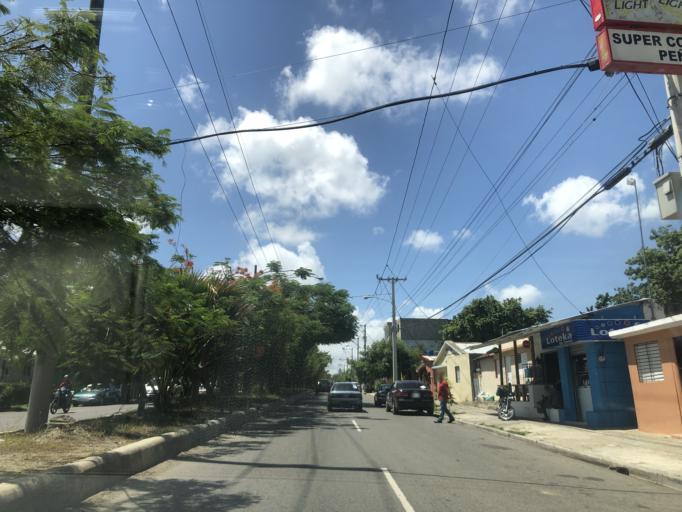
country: DO
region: Santiago
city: Santiago de los Caballeros
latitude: 19.4476
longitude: -70.7426
